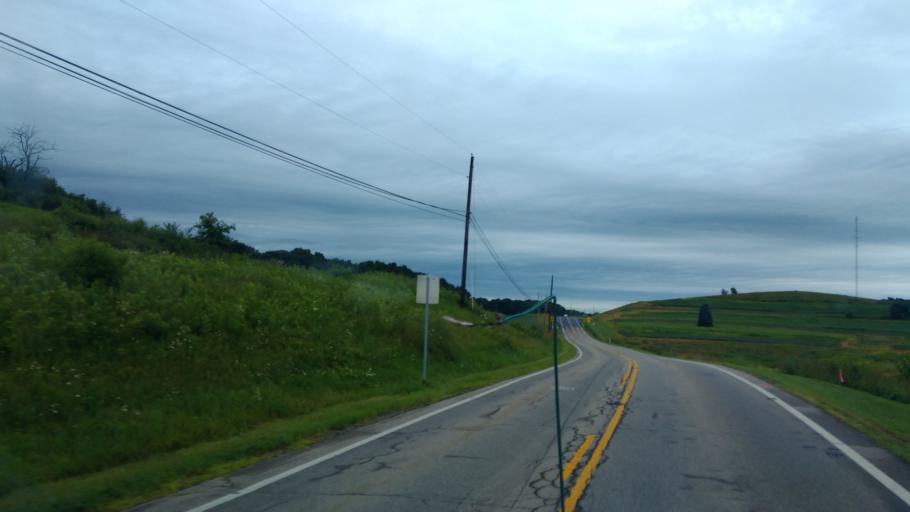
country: US
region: Ohio
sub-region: Carroll County
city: Carrollton
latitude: 40.6150
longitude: -81.0674
